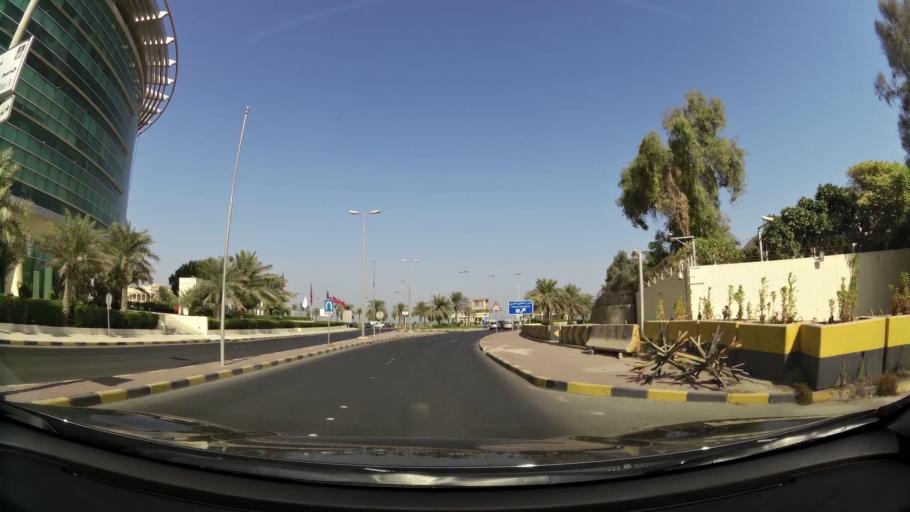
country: KW
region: Al Asimah
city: Kuwait City
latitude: 29.3896
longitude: 47.9942
